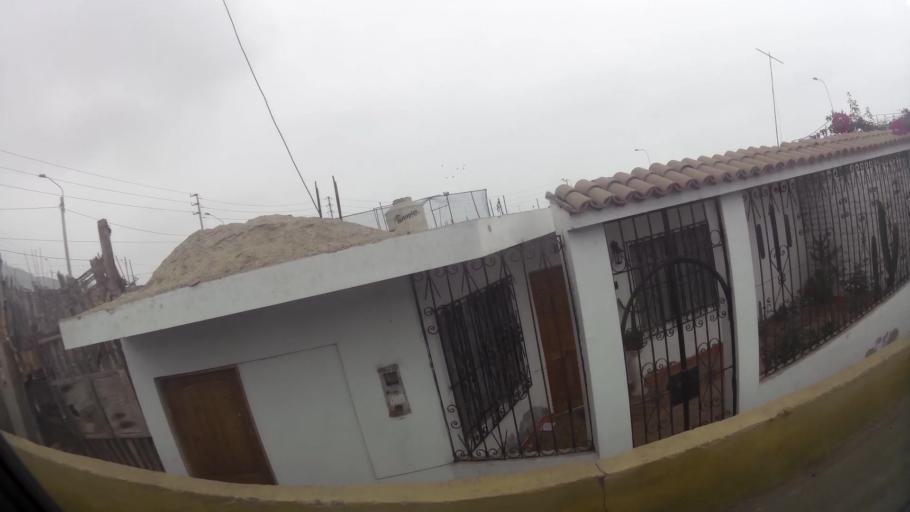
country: PE
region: Lima
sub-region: Provincia de Huaral
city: Chancay
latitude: -11.5930
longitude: -77.2557
